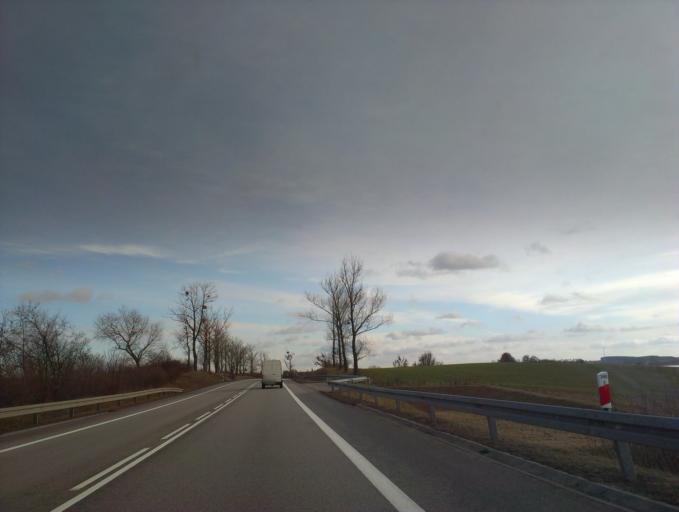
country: PL
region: Kujawsko-Pomorskie
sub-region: Powiat lipnowski
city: Kikol
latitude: 52.9232
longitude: 19.0918
